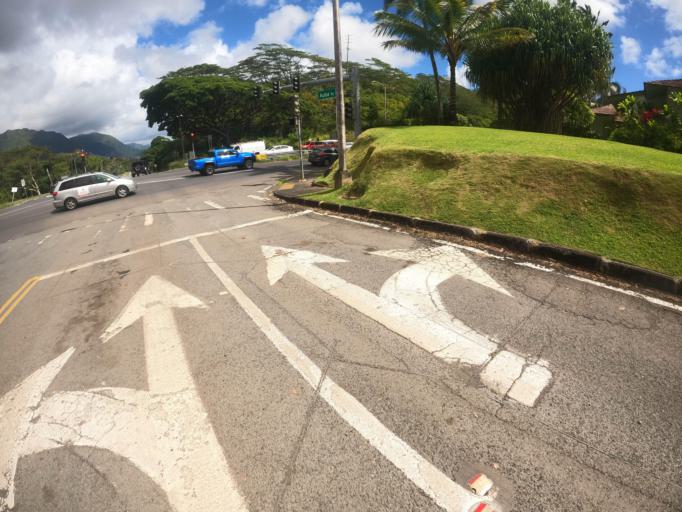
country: US
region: Hawaii
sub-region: Honolulu County
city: Maunawili
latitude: 21.3749
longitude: -157.7806
